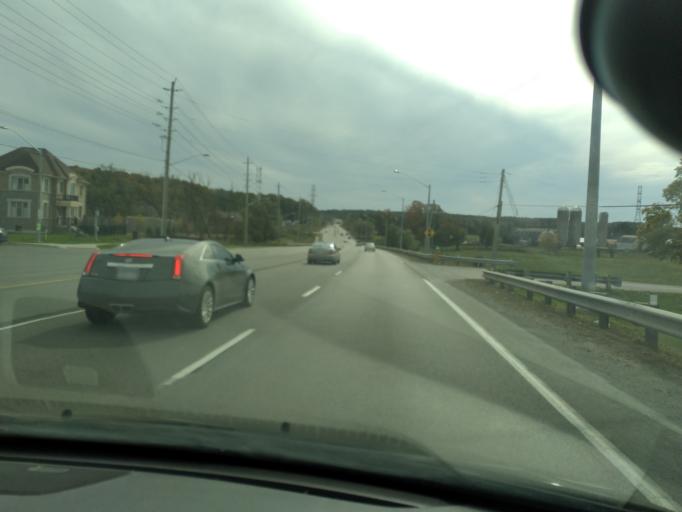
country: CA
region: Ontario
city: Newmarket
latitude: 44.0586
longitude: -79.5085
